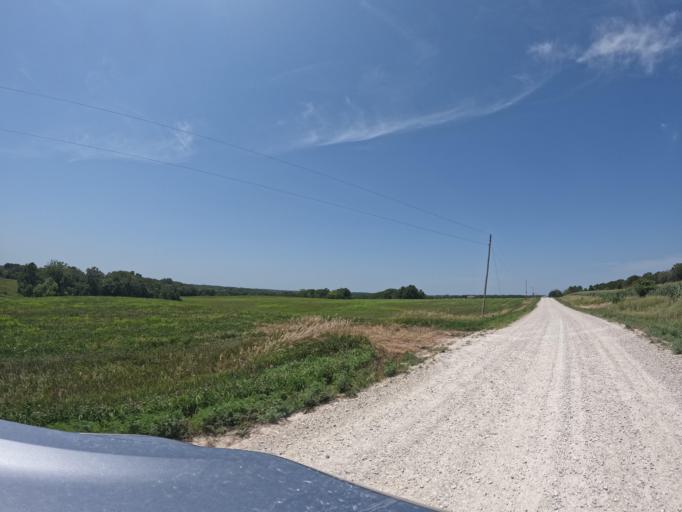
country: US
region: Iowa
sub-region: Henry County
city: Mount Pleasant
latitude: 40.9118
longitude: -91.6554
